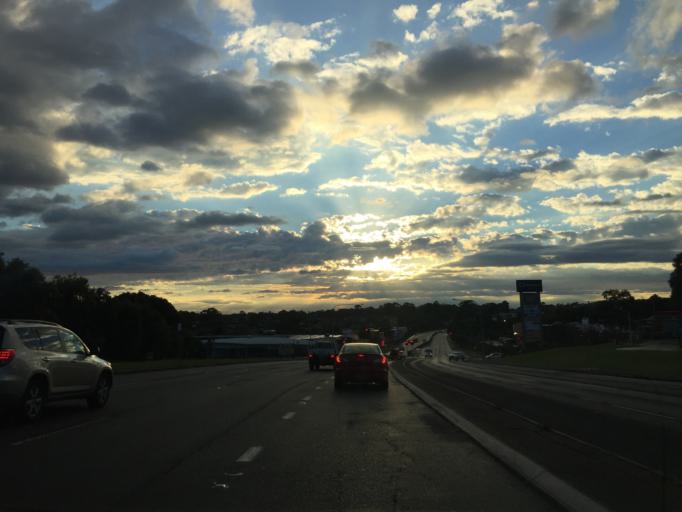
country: AU
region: New South Wales
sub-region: Shellharbour
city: Barrack Heights
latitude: -34.5646
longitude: 150.8287
